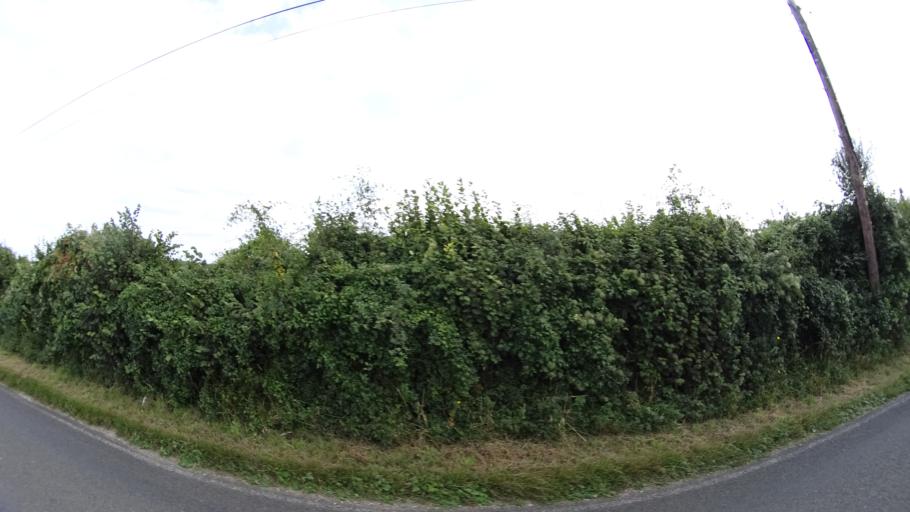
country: GB
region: England
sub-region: Dorset
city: Three Legged Cross
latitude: 50.8804
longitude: -1.9741
